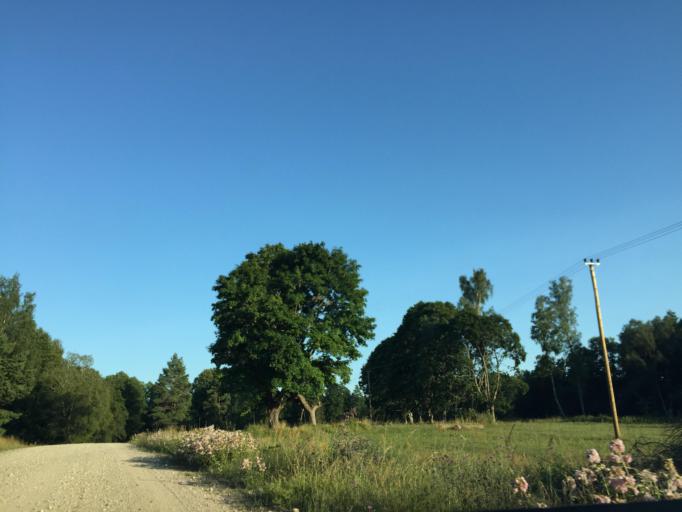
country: LV
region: Talsu Rajons
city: Stende
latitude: 57.1557
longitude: 22.2936
